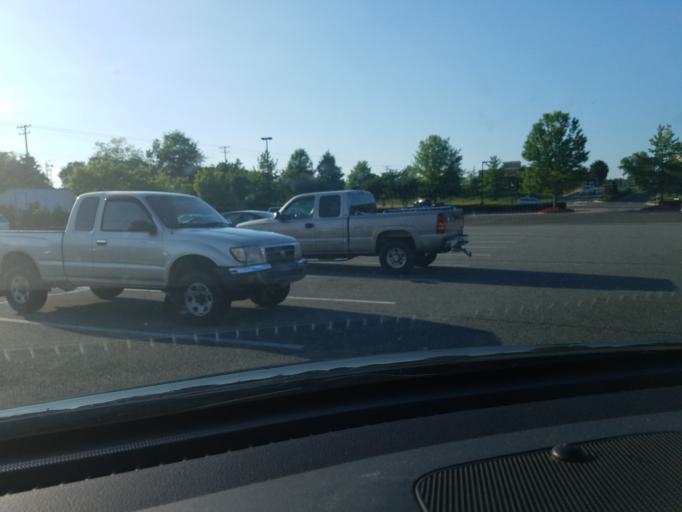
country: US
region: North Carolina
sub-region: Orange County
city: Chapel Hill
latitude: 35.9501
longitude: -78.9934
